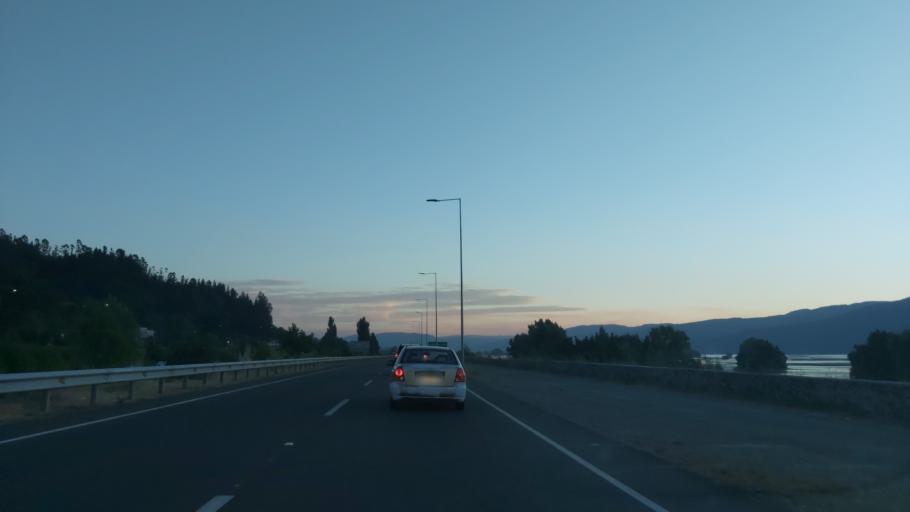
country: CL
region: Biobio
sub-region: Provincia de Concepcion
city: Chiguayante
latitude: -36.8816
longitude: -73.0388
